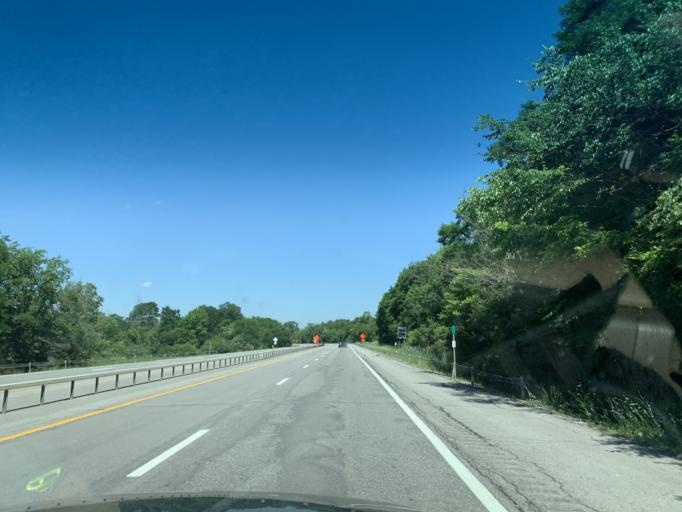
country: US
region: New York
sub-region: Oneida County
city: Chadwicks
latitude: 43.0122
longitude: -75.2547
